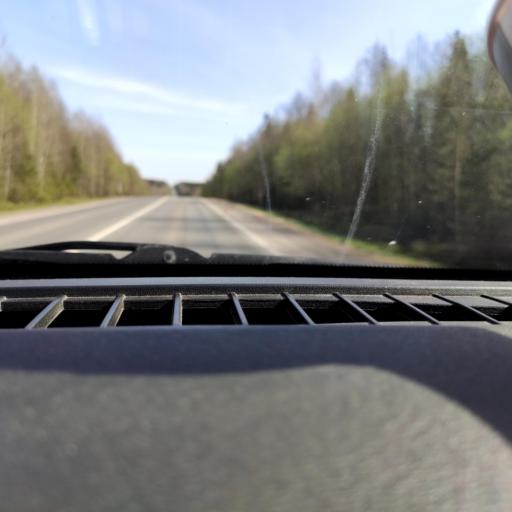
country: RU
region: Perm
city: Perm
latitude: 58.1697
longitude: 56.2358
